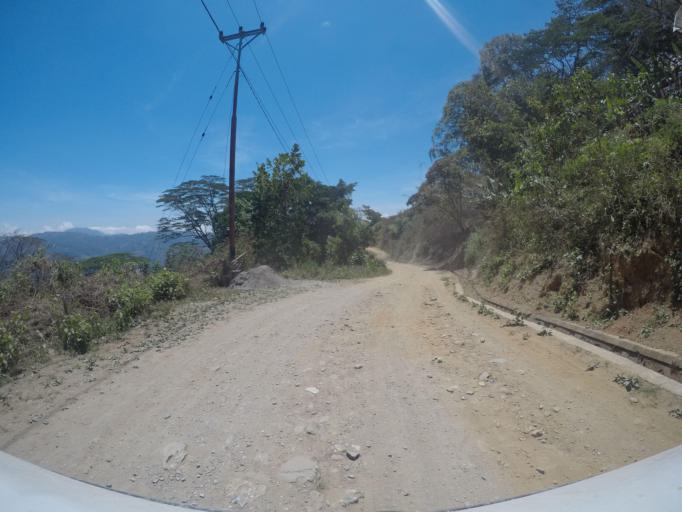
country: TL
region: Ermera
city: Gleno
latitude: -8.7441
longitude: 125.4023
